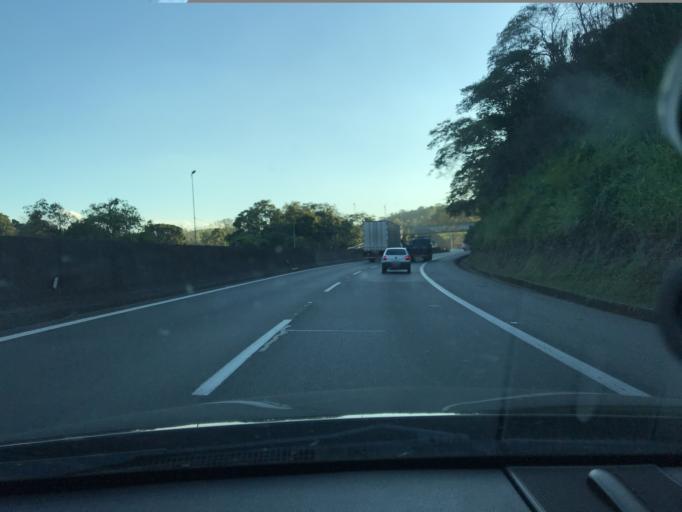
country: BR
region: Sao Paulo
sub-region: Cajamar
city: Cajamar
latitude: -23.3088
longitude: -46.8563
